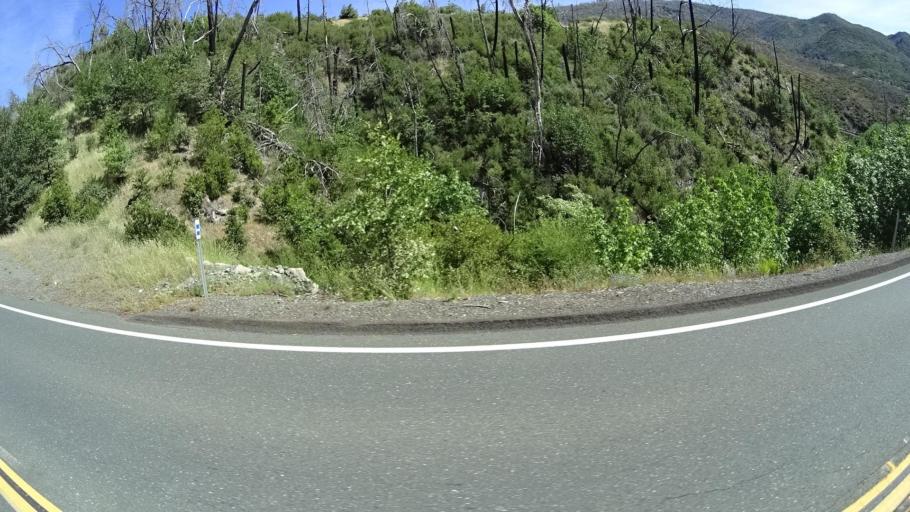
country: US
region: California
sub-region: Lake County
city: Cobb
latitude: 38.7915
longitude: -122.7005
